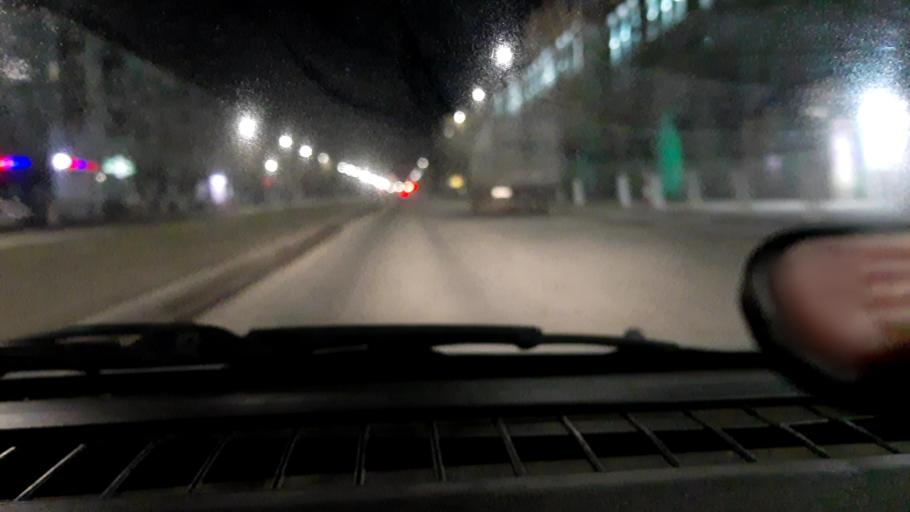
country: RU
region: Nizjnij Novgorod
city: Dzerzhinsk
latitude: 56.2410
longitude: 43.4482
